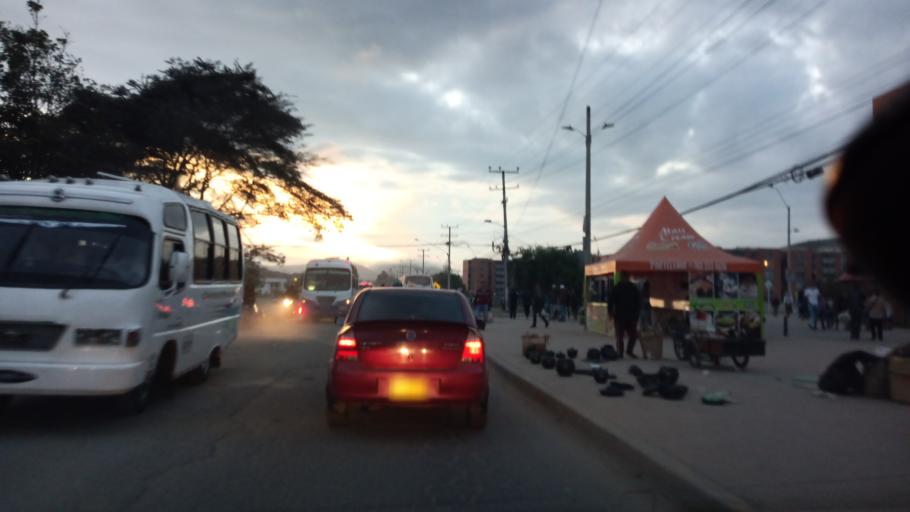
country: CO
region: Cundinamarca
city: Soacha
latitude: 4.5827
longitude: -74.2252
